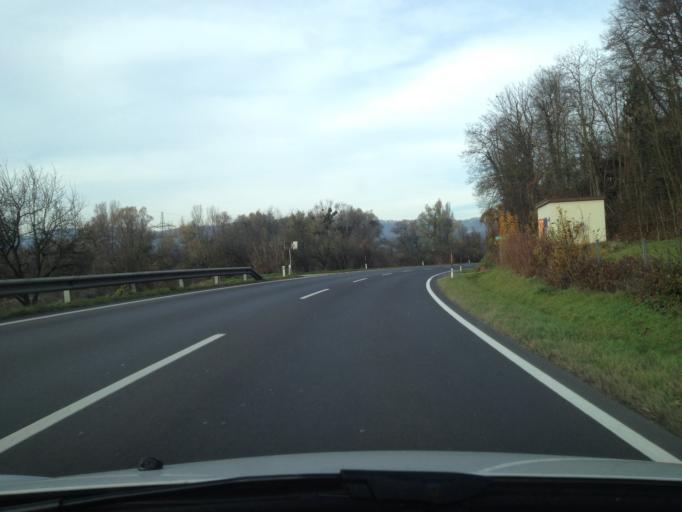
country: AT
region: Upper Austria
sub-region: Politischer Bezirk Urfahr-Umgebung
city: Steyregg
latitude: 48.3121
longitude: 14.3353
